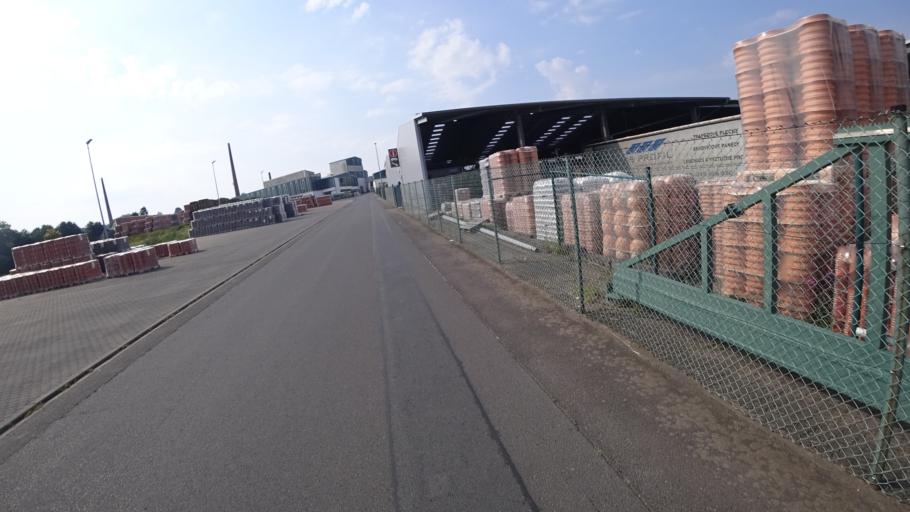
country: DE
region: Rheinland-Pfalz
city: Hundsdorf
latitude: 50.4619
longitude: 7.7206
